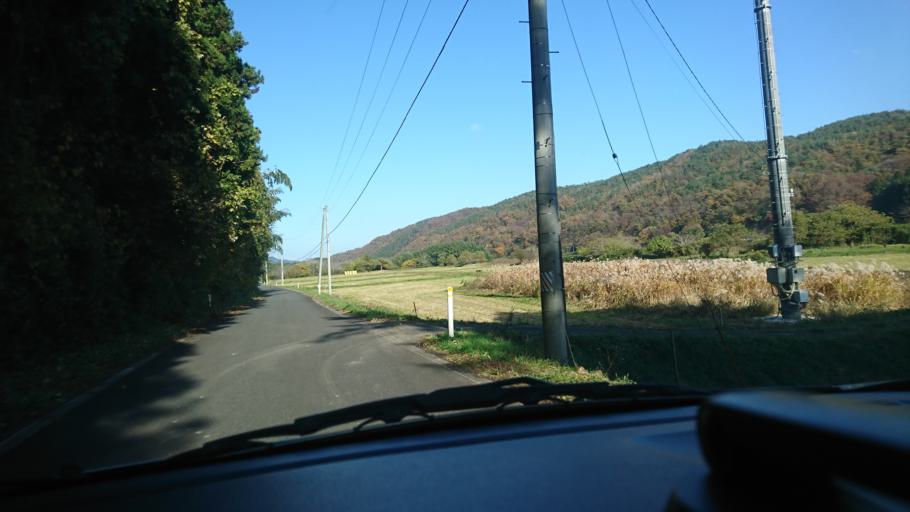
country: JP
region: Iwate
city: Ichinoseki
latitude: 38.8061
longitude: 141.2459
